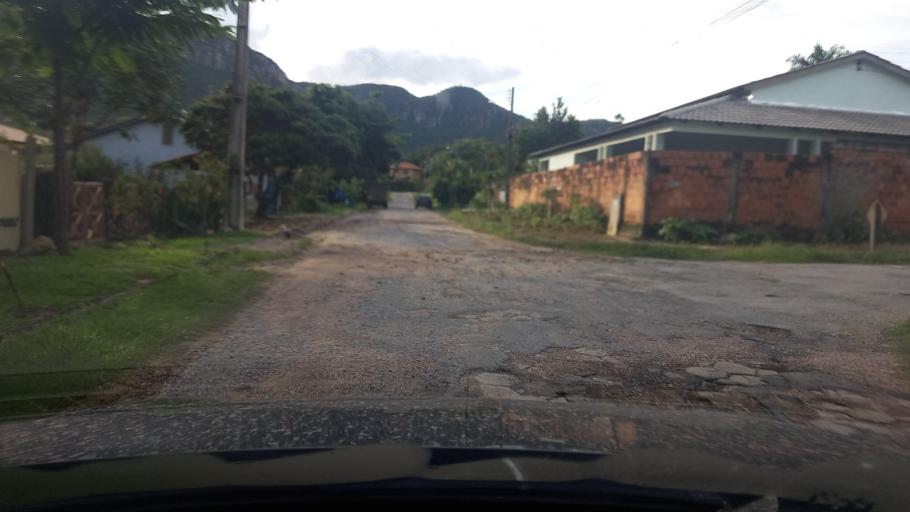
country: BR
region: Goias
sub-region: Cavalcante
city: Cavalcante
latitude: -13.7933
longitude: -47.4626
